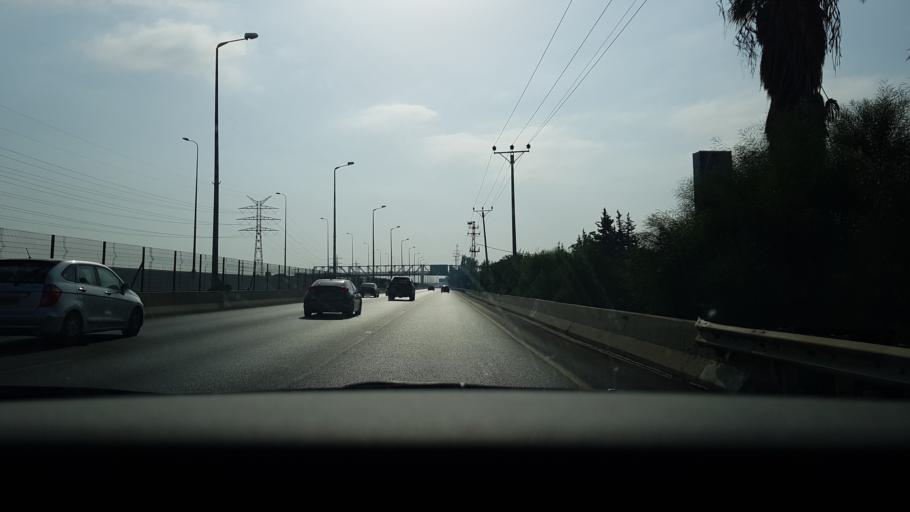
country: IL
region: Tel Aviv
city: Azor
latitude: 32.0308
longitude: 34.8035
